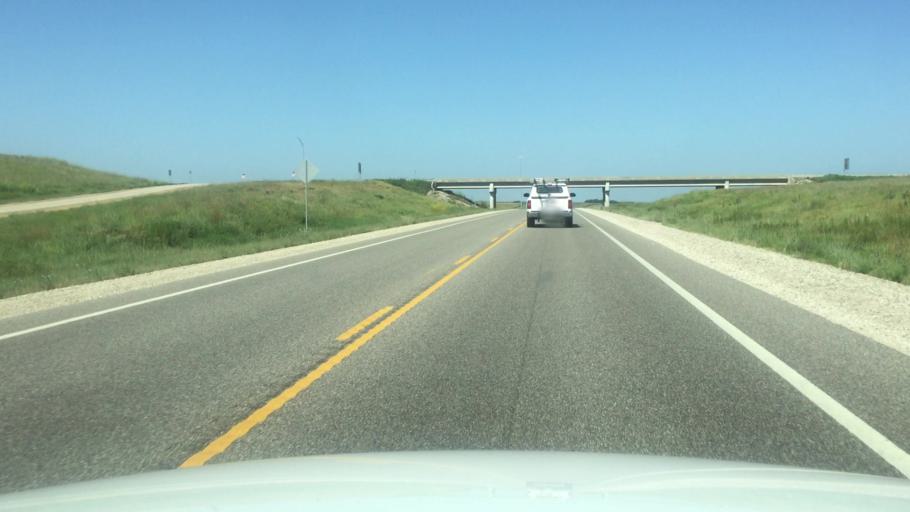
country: US
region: Kansas
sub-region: Doniphan County
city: Troy
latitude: 39.7981
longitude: -95.1404
